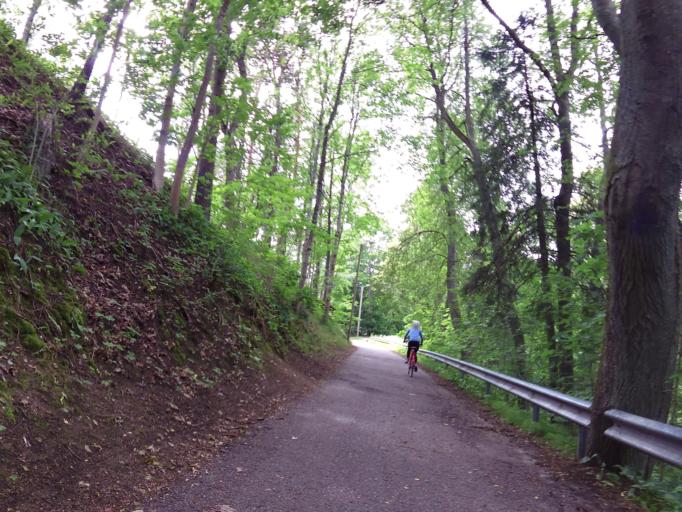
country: EE
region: Harju
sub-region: Saue vald
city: Laagri
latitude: 59.3885
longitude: 24.6579
